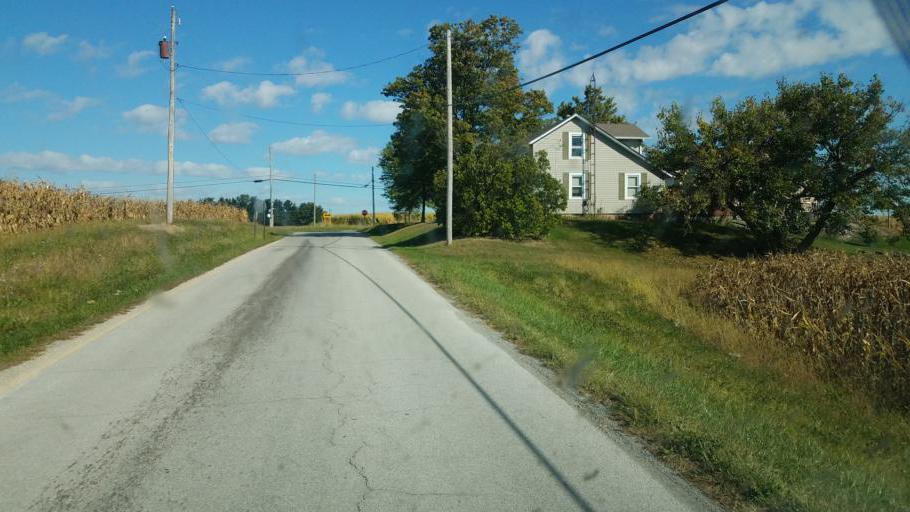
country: US
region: Ohio
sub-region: Wyandot County
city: Upper Sandusky
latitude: 40.8247
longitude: -83.2462
